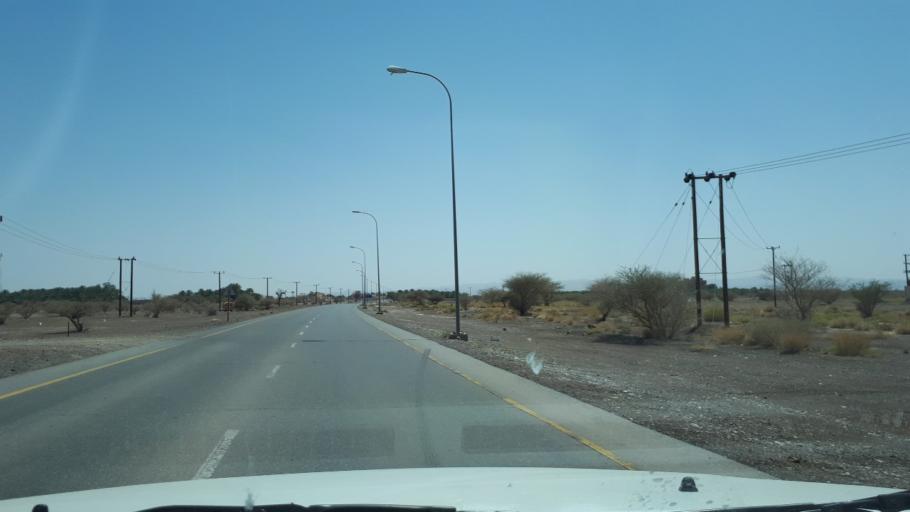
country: OM
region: Muhafazat ad Dakhiliyah
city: Bahla'
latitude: 22.9214
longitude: 57.2551
